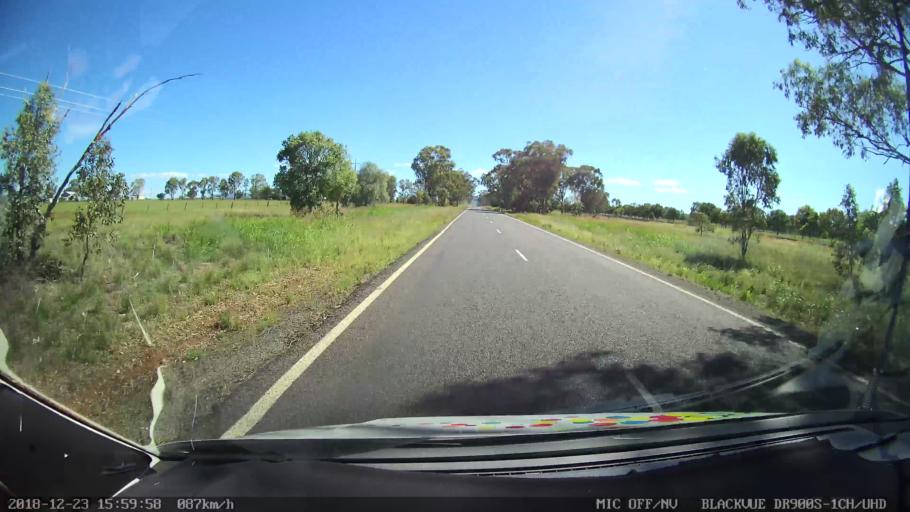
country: AU
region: New South Wales
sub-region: Tamworth Municipality
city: Phillip
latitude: -31.2056
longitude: 150.8289
